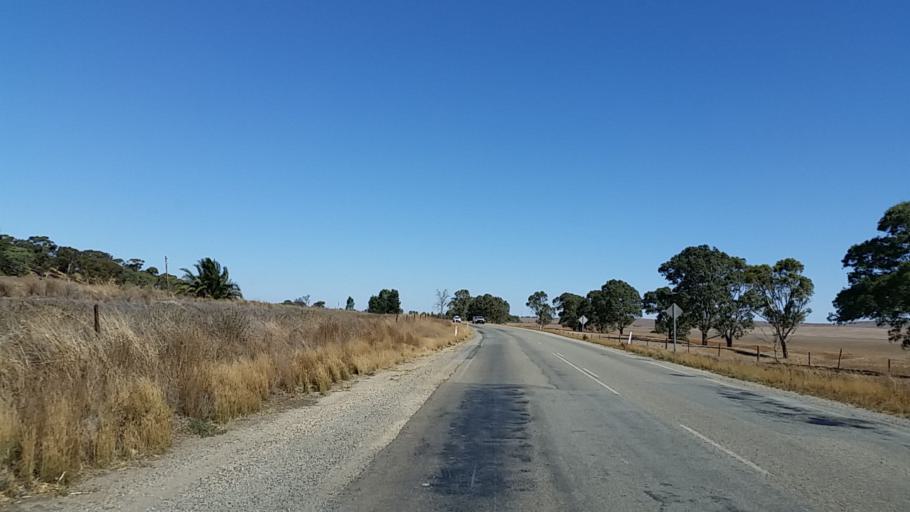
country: AU
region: South Australia
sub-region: Clare and Gilbert Valleys
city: Clare
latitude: -33.6777
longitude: 138.9146
